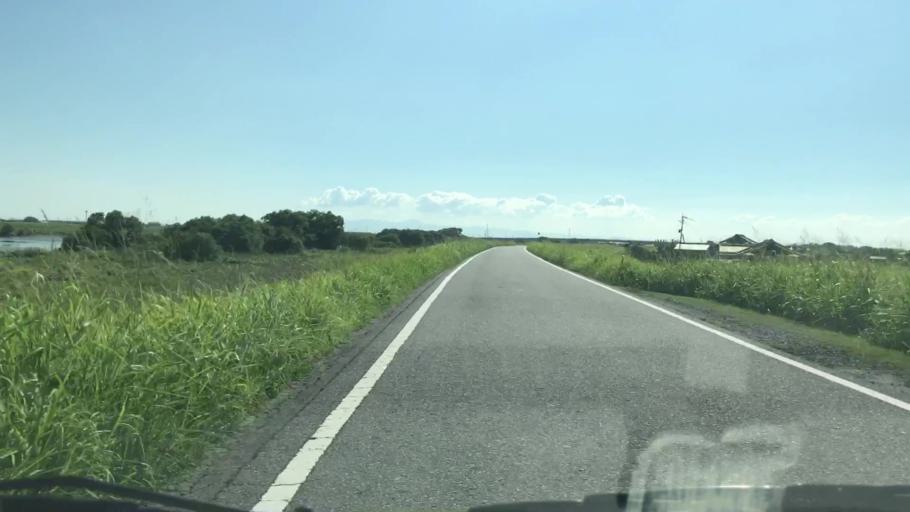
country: JP
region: Saga Prefecture
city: Kanzakimachi-kanzaki
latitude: 33.2766
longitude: 130.4441
